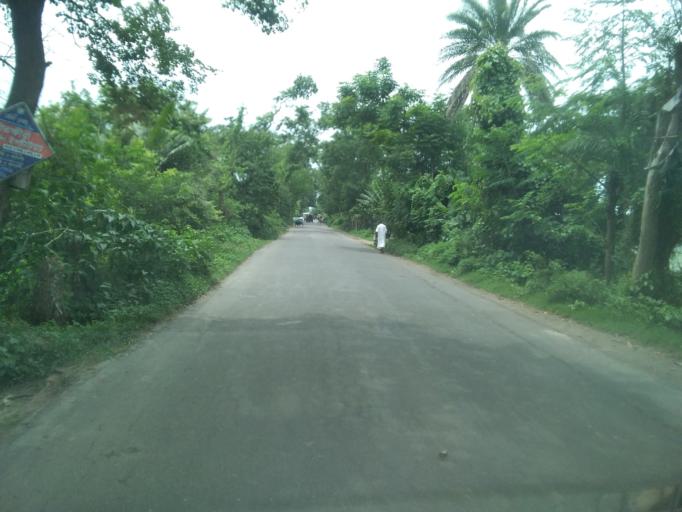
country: IN
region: West Bengal
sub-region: North 24 Parganas
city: Taki
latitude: 22.5761
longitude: 88.9990
